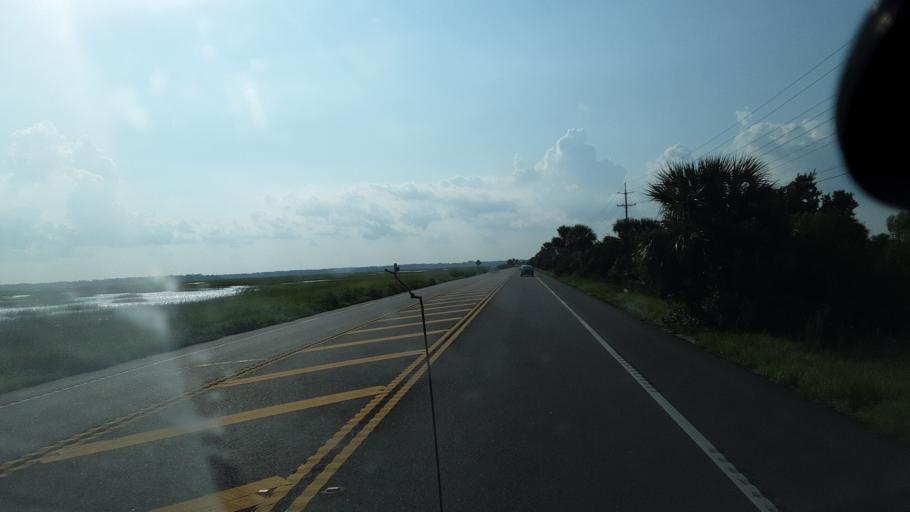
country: US
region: Georgia
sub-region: Chatham County
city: Tybee Island
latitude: 32.0220
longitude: -80.9084
